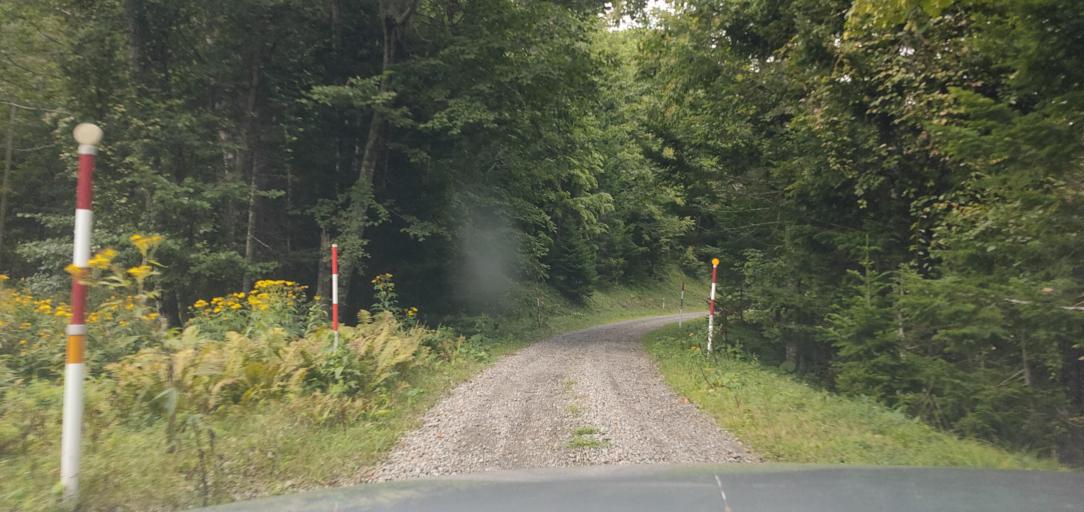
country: JP
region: Hokkaido
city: Kitami
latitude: 43.3676
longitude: 143.9360
